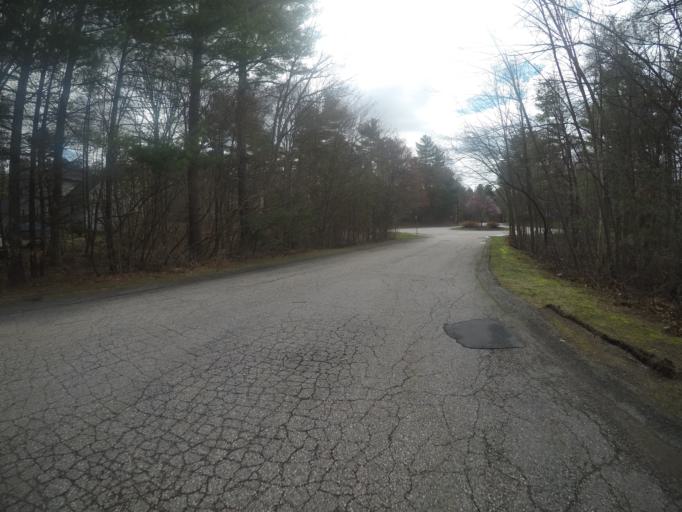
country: US
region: Massachusetts
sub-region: Bristol County
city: Easton
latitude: 42.0422
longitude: -71.1315
